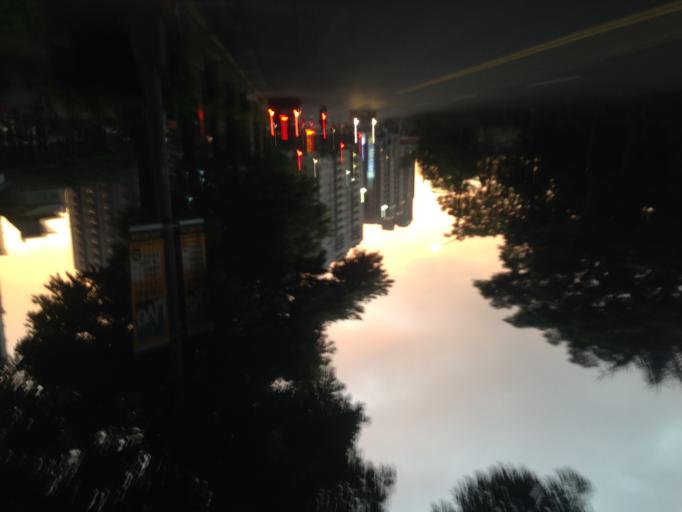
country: TW
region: Taiwan
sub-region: Taoyuan
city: Taoyuan
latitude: 24.9405
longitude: 121.3746
